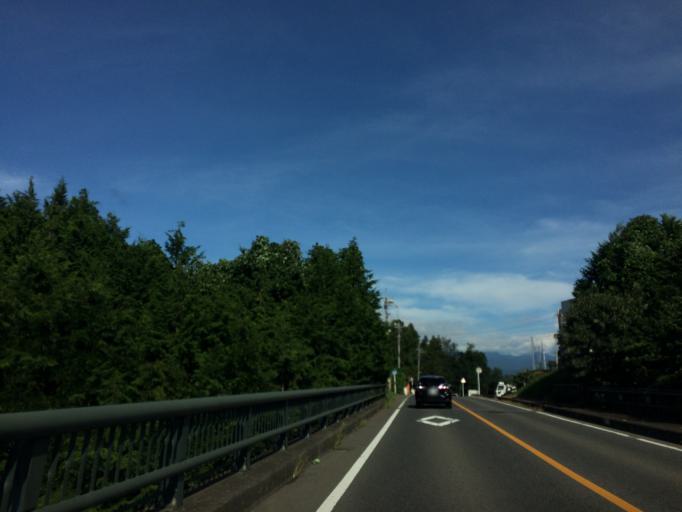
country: JP
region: Gunma
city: Nakanojomachi
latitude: 36.5488
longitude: 138.9179
